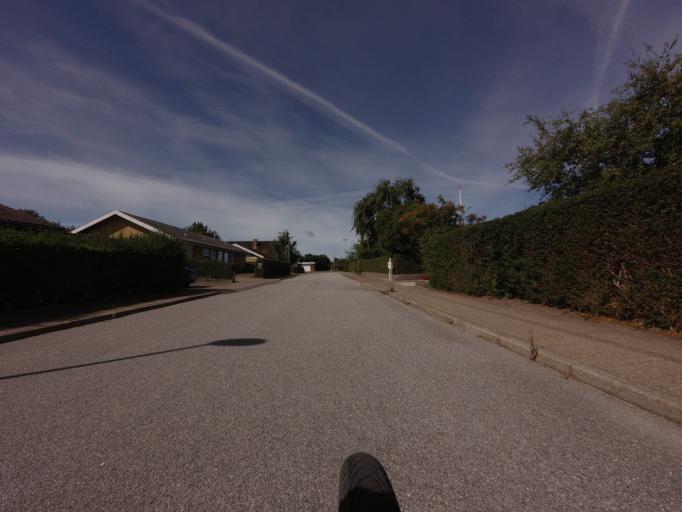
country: DK
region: North Denmark
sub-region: Jammerbugt Kommune
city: Pandrup
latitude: 57.3399
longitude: 9.7744
